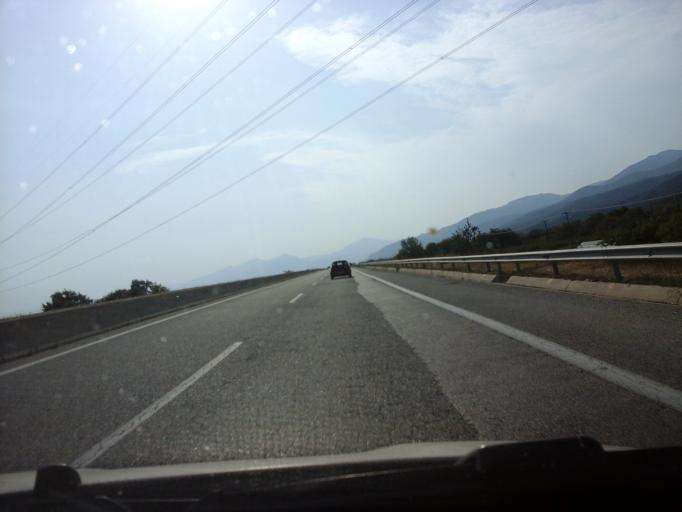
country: GR
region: East Macedonia and Thrace
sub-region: Nomos Rodopis
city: Iasmos
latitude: 41.1183
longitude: 25.0982
